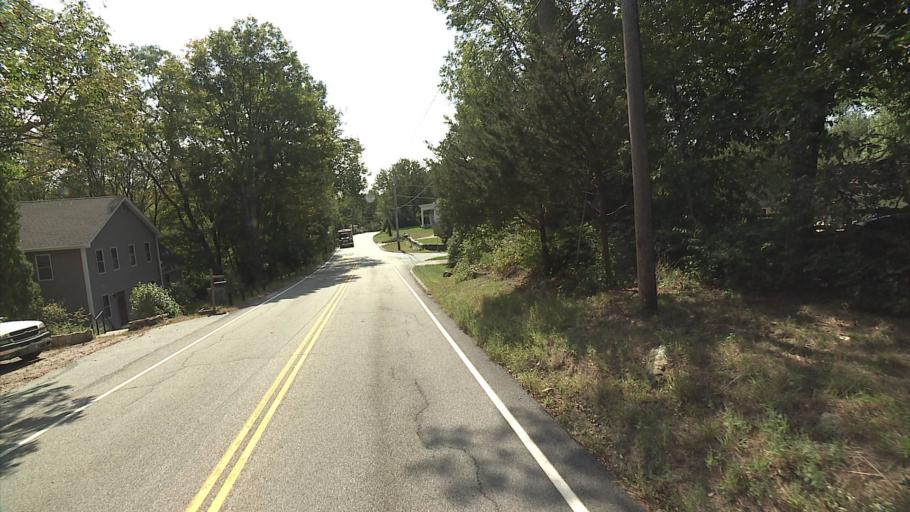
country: US
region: Connecticut
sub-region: Windham County
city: Plainfield Village
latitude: 41.7058
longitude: -71.9683
